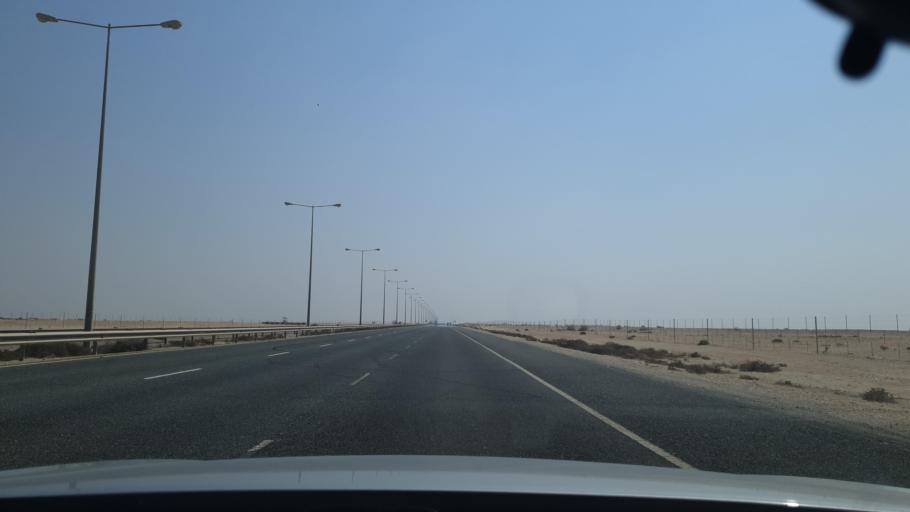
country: QA
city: Al Ghuwayriyah
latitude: 25.8058
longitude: 51.3781
